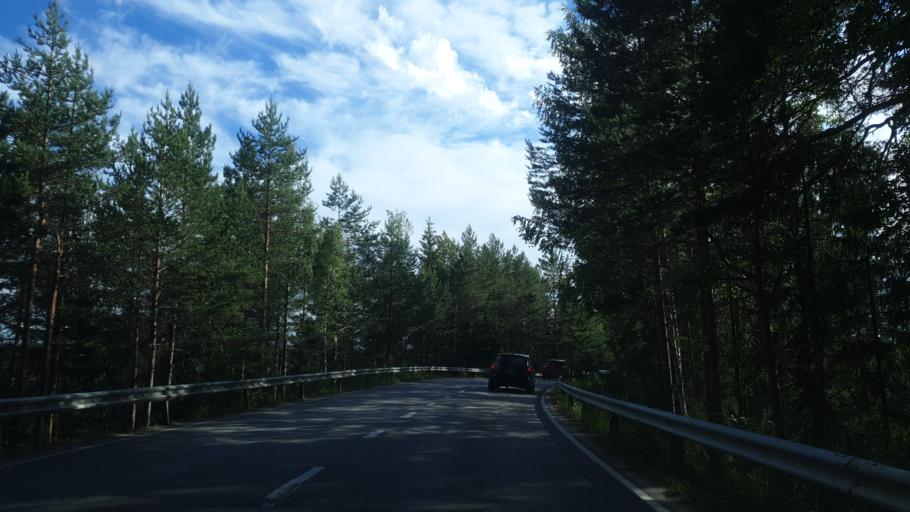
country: FI
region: Southern Savonia
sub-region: Mikkeli
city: Pertunmaa
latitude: 61.4929
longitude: 26.4768
